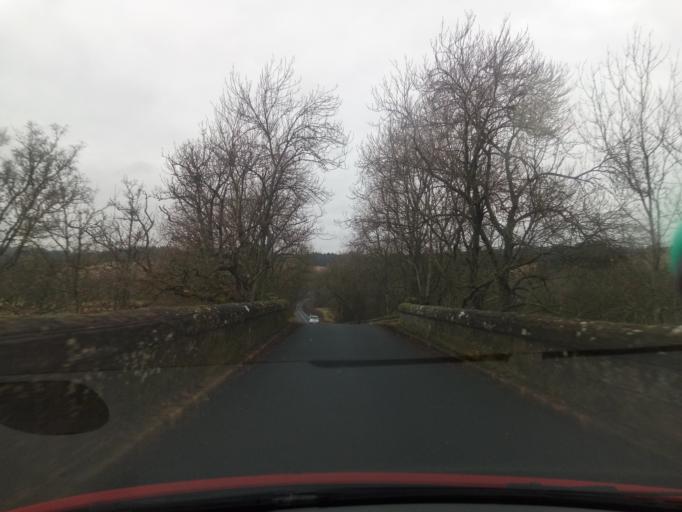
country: GB
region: England
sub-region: Northumberland
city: Rochester
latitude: 55.1776
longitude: -2.4370
